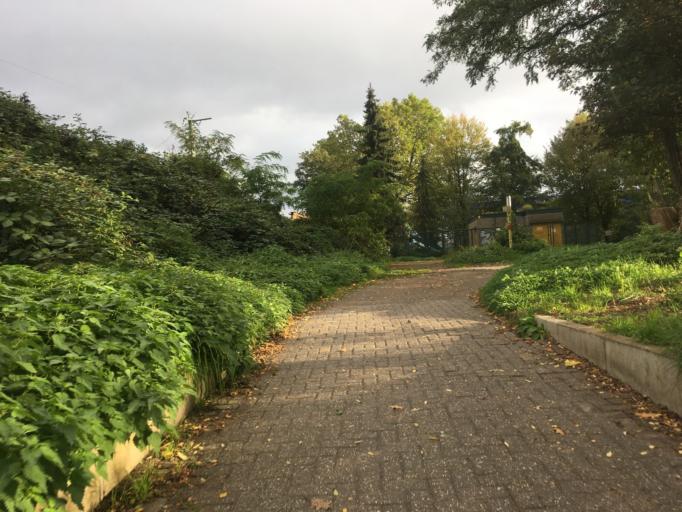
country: DE
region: North Rhine-Westphalia
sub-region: Regierungsbezirk Dusseldorf
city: Oberhausen
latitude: 51.4921
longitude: 6.8498
